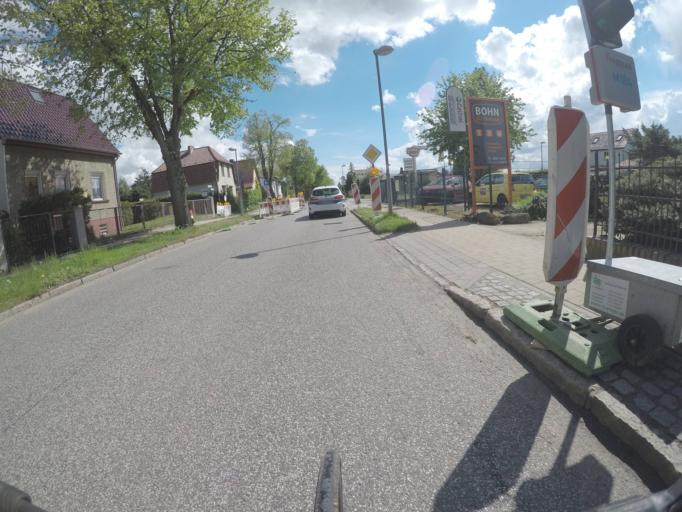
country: DE
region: Brandenburg
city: Bernau bei Berlin
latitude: 52.6998
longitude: 13.5882
